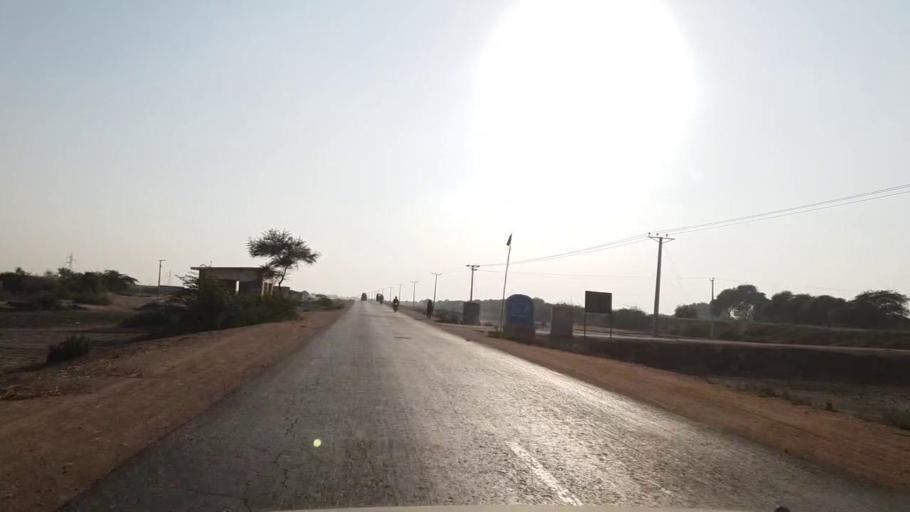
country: PK
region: Sindh
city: Mirpur Batoro
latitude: 24.7578
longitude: 68.2713
